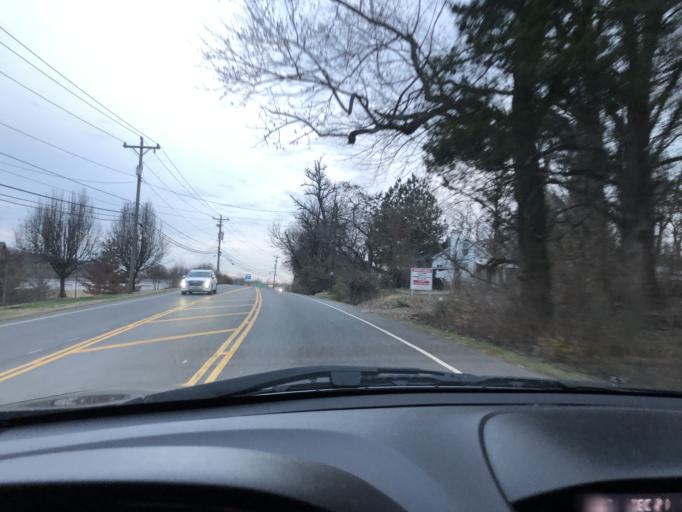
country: US
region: Tennessee
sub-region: Wilson County
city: Green Hill
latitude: 36.1726
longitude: -86.5964
